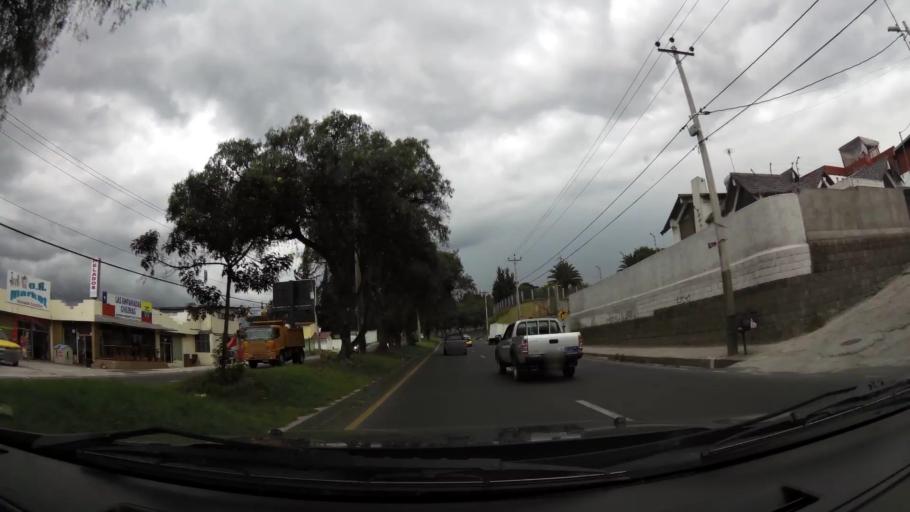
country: EC
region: Pichincha
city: Quito
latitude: -0.0641
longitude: -78.4570
